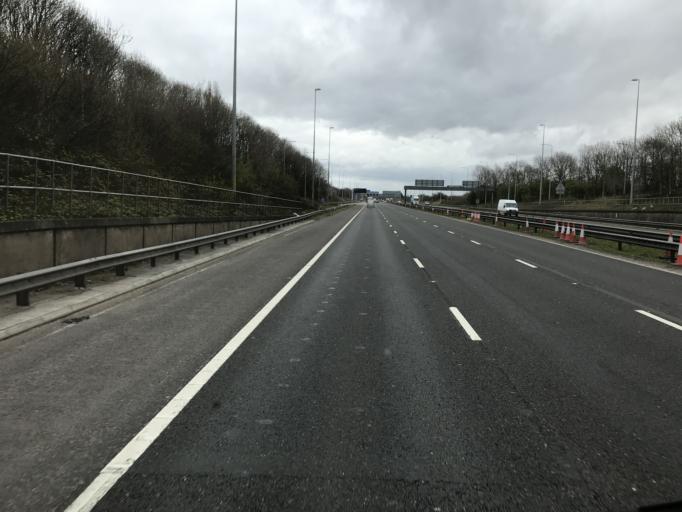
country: GB
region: England
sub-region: Warrington
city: Winwick
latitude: 53.4227
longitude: -2.5959
